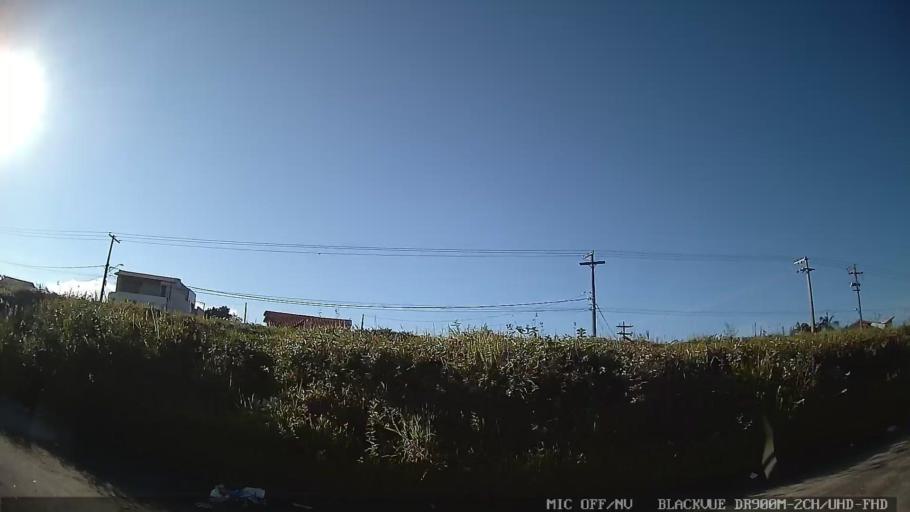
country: BR
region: Sao Paulo
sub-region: Peruibe
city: Peruibe
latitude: -24.2985
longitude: -46.9836
